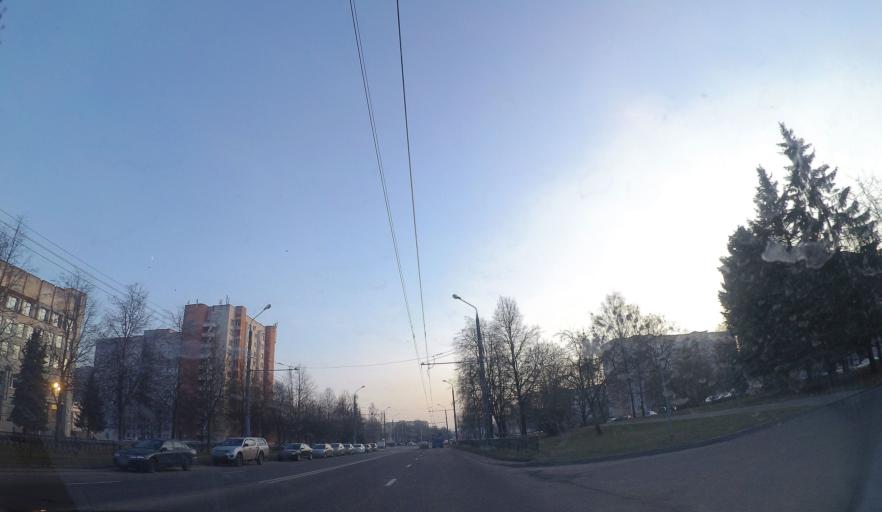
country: BY
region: Grodnenskaya
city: Hrodna
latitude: 53.6999
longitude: 23.8080
